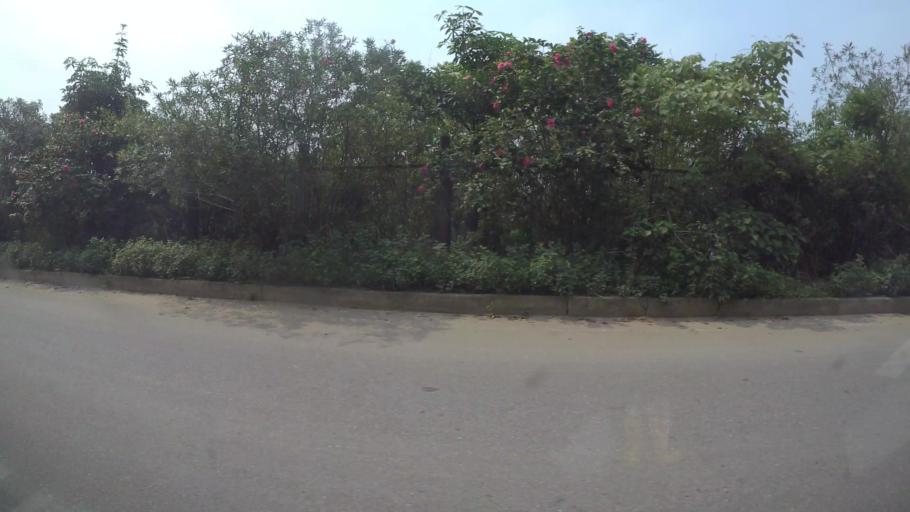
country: VN
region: Ha Noi
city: Lien Quan
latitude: 20.9904
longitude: 105.5579
